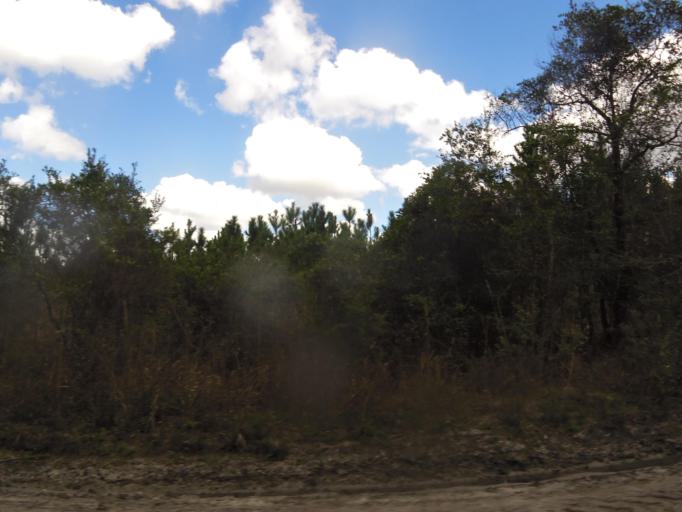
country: US
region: Florida
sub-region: Clay County
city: Green Cove Springs
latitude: 29.8371
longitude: -81.7526
